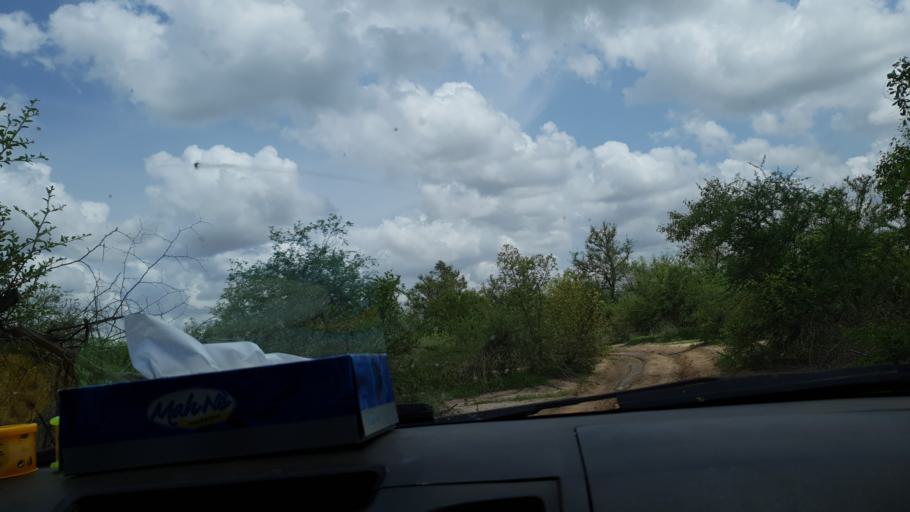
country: ML
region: Segou
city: Baroueli
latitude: 13.3542
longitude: -7.0973
